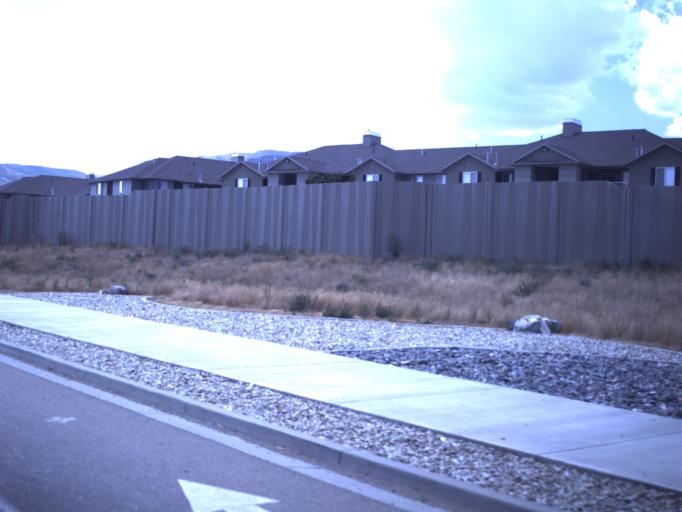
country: US
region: Utah
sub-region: Salt Lake County
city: Herriman
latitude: 40.5076
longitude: -112.0052
